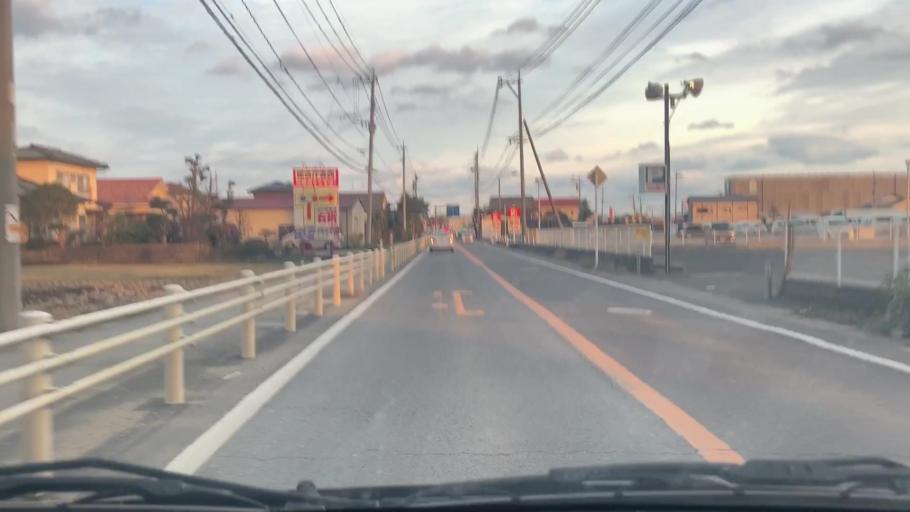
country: JP
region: Saga Prefecture
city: Kashima
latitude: 33.1225
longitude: 130.0929
